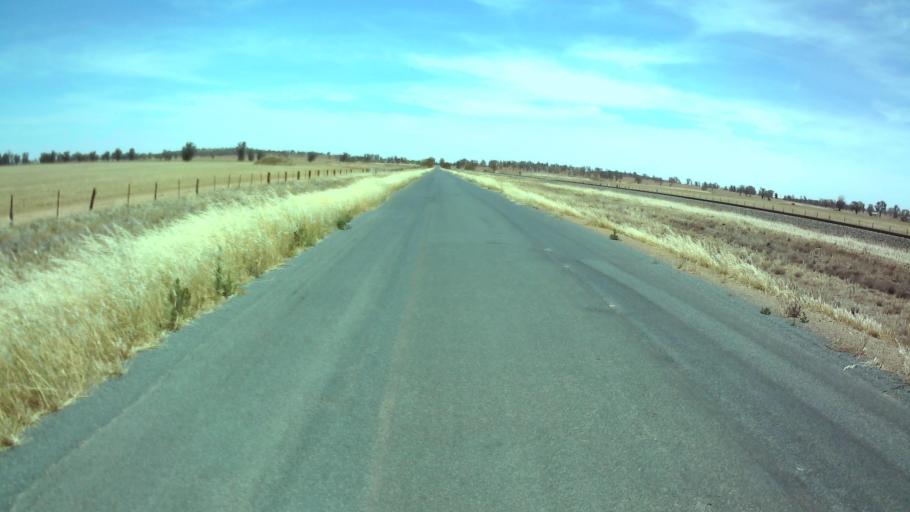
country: AU
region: New South Wales
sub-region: Weddin
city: Grenfell
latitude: -33.7561
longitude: 147.7630
